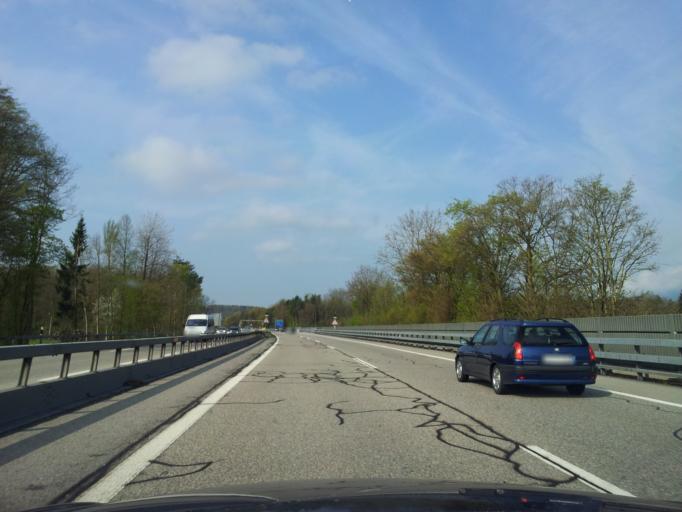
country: CH
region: Solothurn
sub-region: Bezirk Wasseramt
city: Luterbach
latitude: 47.2089
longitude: 7.5819
